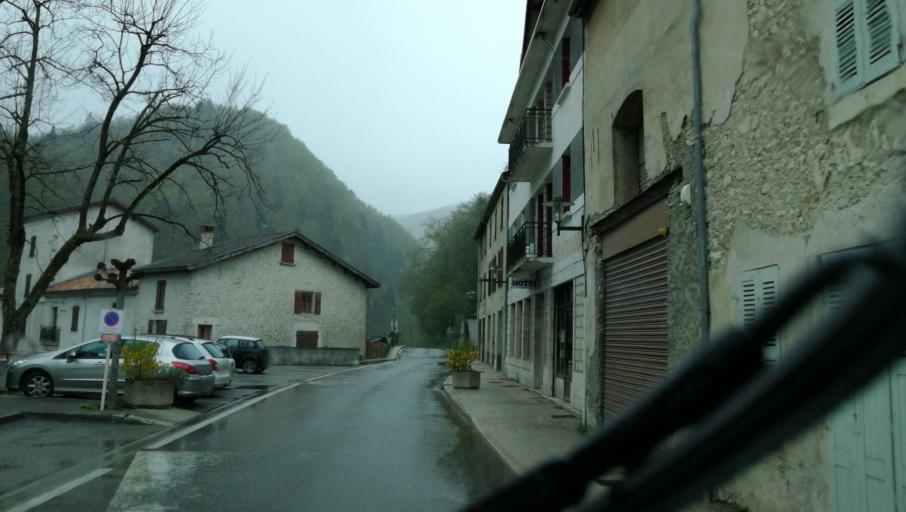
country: FR
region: Rhone-Alpes
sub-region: Departement de l'Isere
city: Meaudre
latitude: 45.0881
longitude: 5.4678
